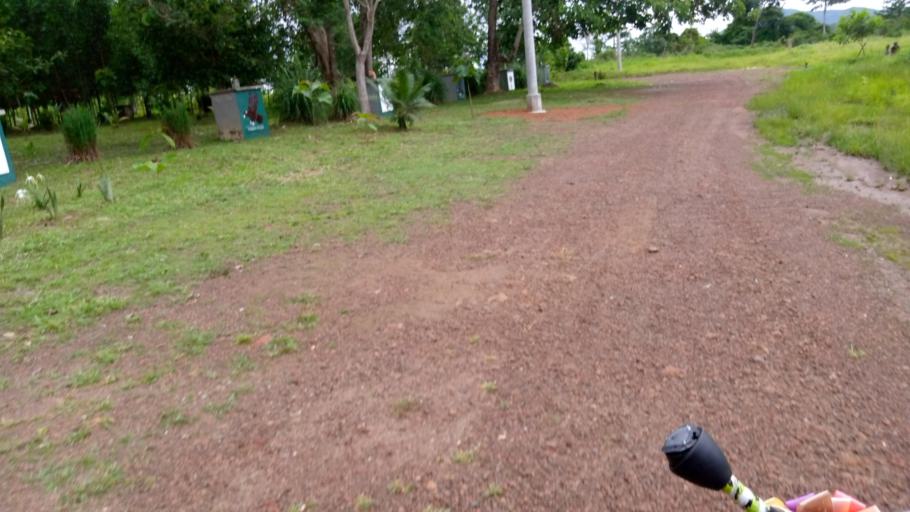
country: SL
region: Southern Province
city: Moyamba
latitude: 8.1585
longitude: -12.4487
